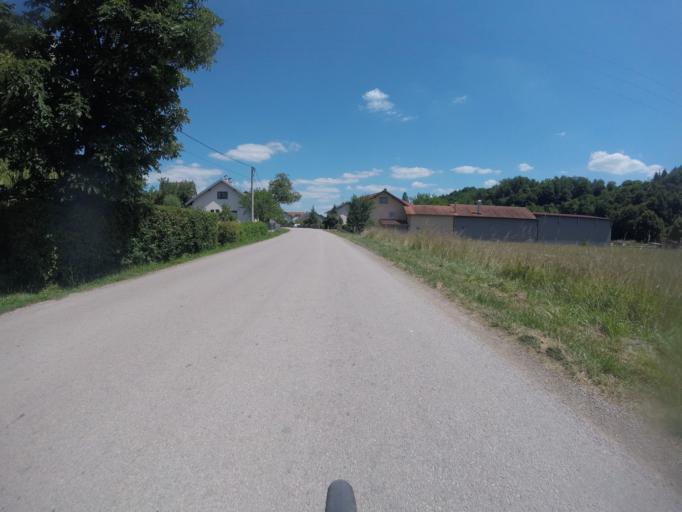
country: HR
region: Karlovacka
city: Ozalj
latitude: 45.6571
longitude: 15.5086
